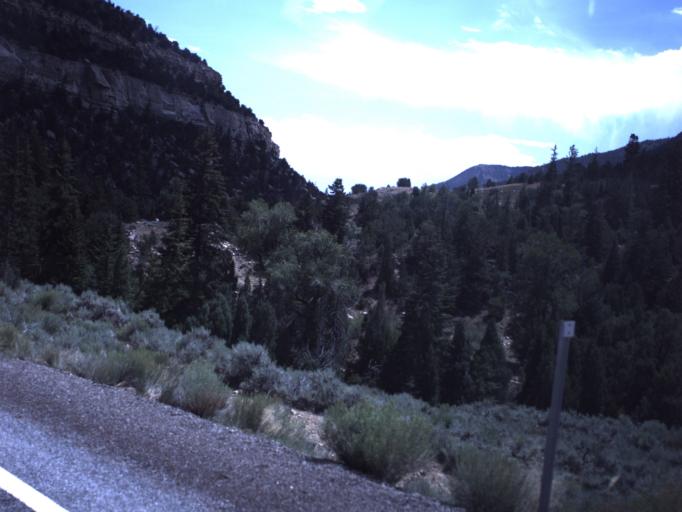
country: US
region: Utah
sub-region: Emery County
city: Huntington
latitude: 39.4253
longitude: -111.1282
